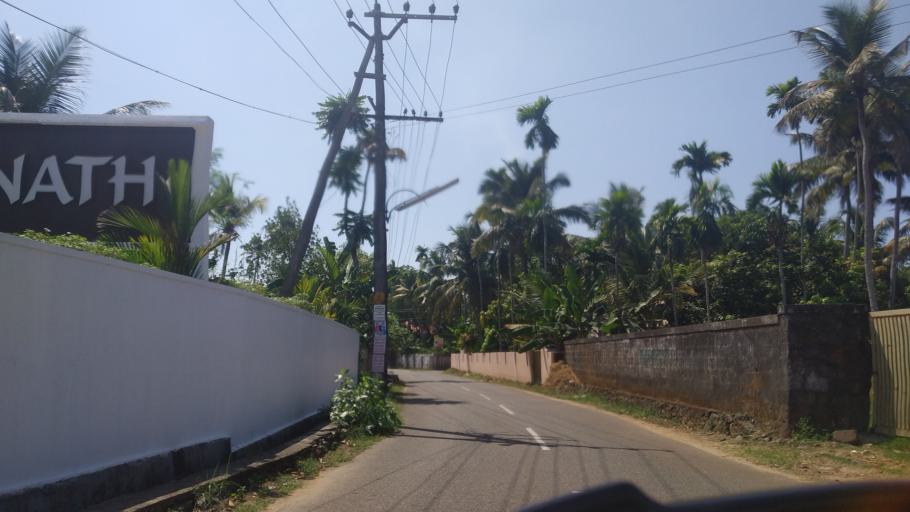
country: IN
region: Kerala
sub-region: Ernakulam
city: Elur
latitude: 10.1331
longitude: 76.2375
